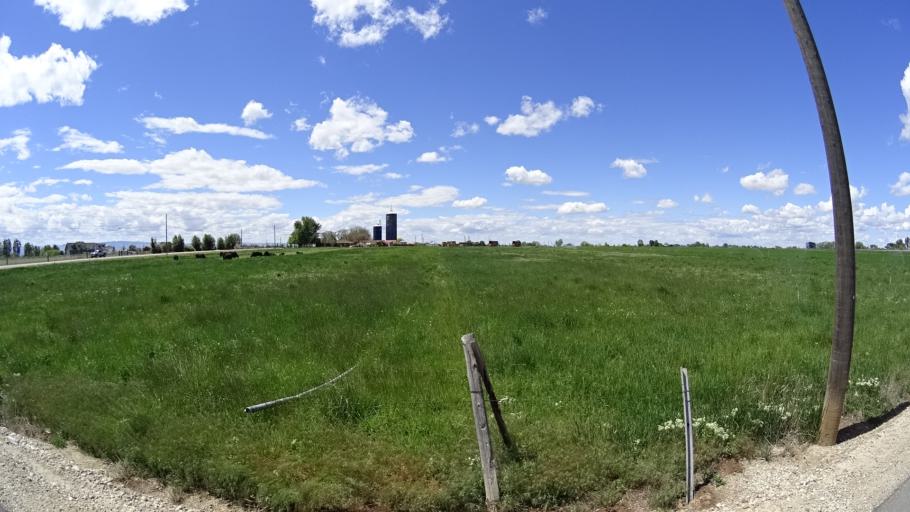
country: US
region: Idaho
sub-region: Ada County
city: Kuna
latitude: 43.5621
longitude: -116.4536
